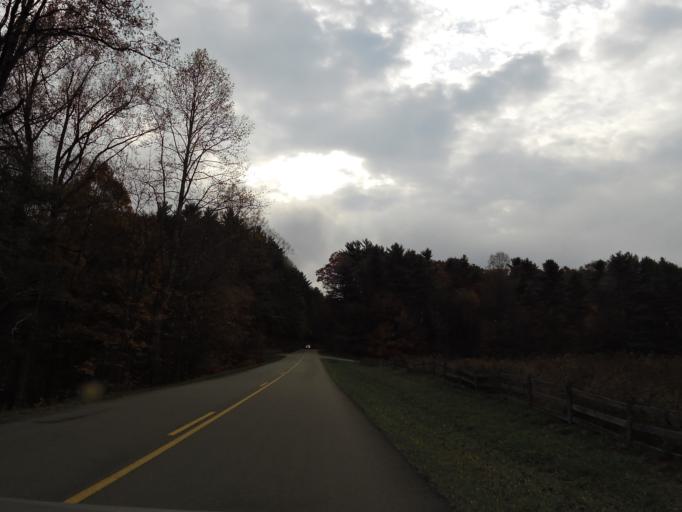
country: US
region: North Carolina
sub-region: Ashe County
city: Jefferson
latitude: 36.3693
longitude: -81.3484
